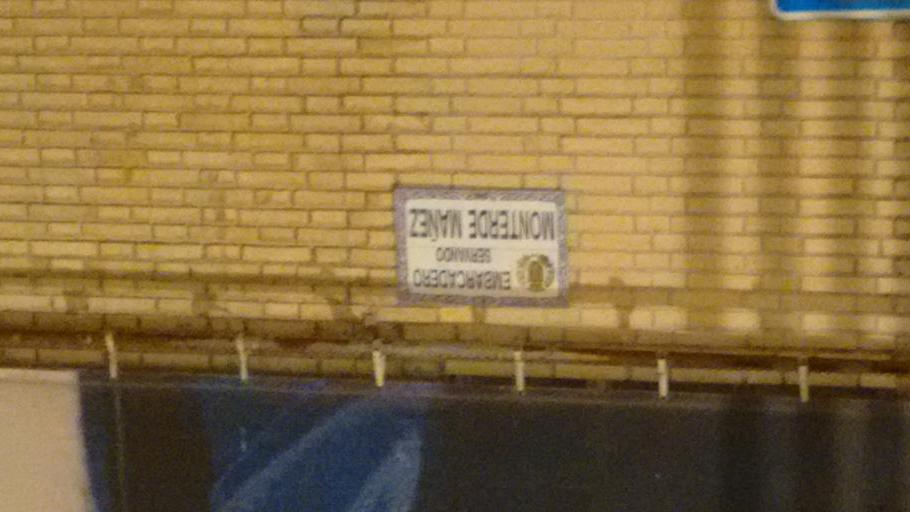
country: ES
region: Aragon
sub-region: Provincia de Zaragoza
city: Zaragoza
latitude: 41.6593
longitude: -0.8824
